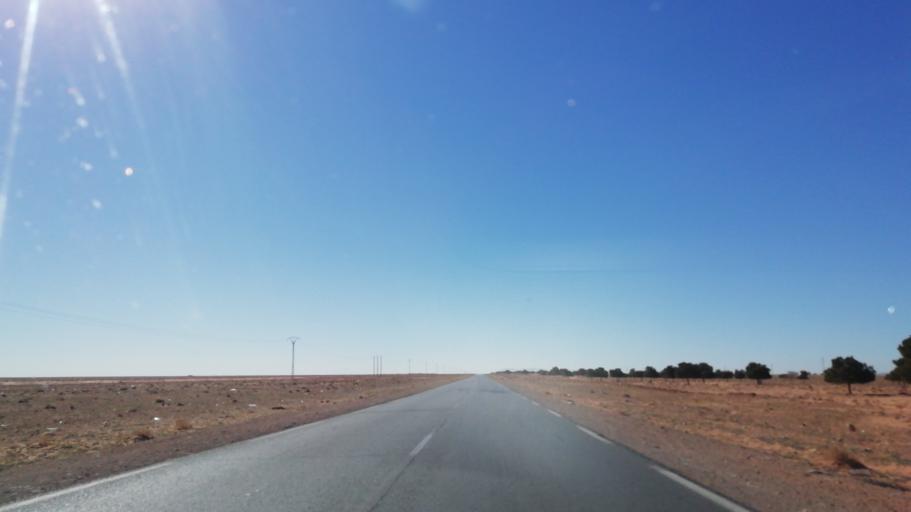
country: DZ
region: Saida
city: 'Ain el Hadjar
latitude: 33.9902
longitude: 0.0353
